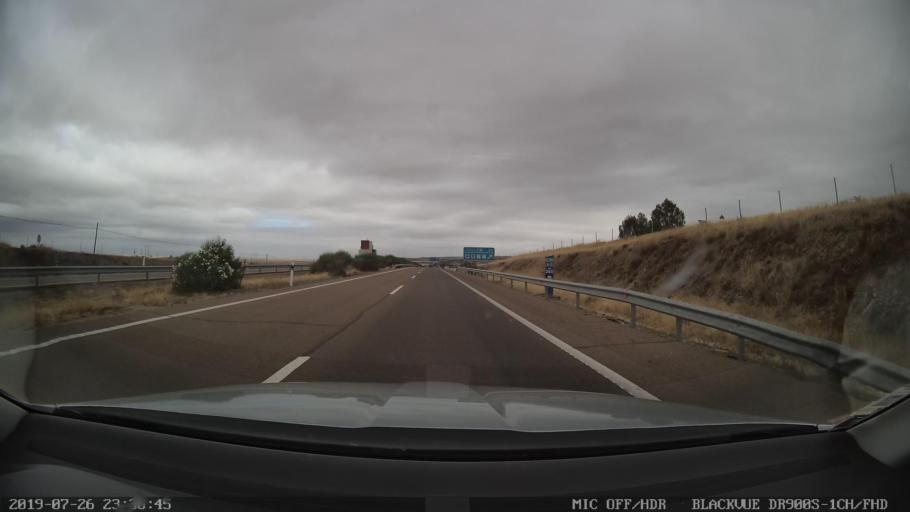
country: ES
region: Extremadura
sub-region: Provincia de Caceres
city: Trujillo
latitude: 39.4000
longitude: -5.8888
